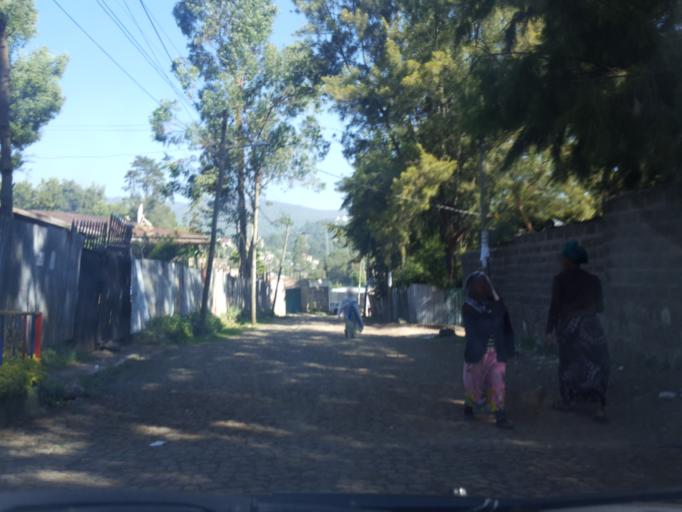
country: ET
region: Adis Abeba
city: Addis Ababa
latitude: 9.0491
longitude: 38.7676
